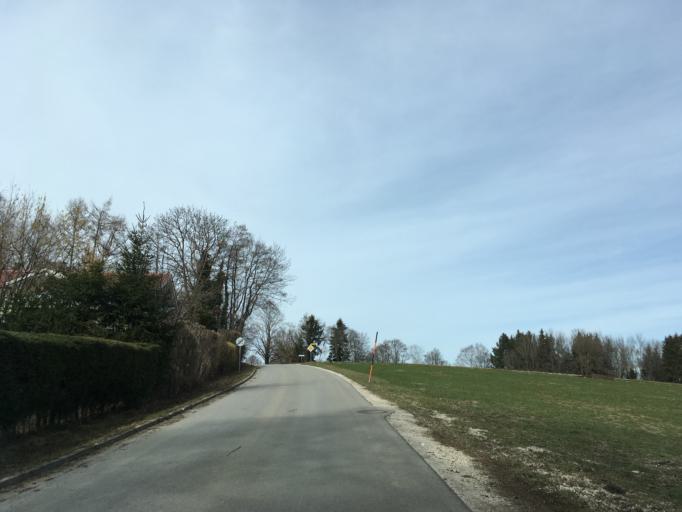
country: DE
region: Bavaria
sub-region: Upper Bavaria
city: Bernau am Chiemsee
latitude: 47.8192
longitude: 12.3442
